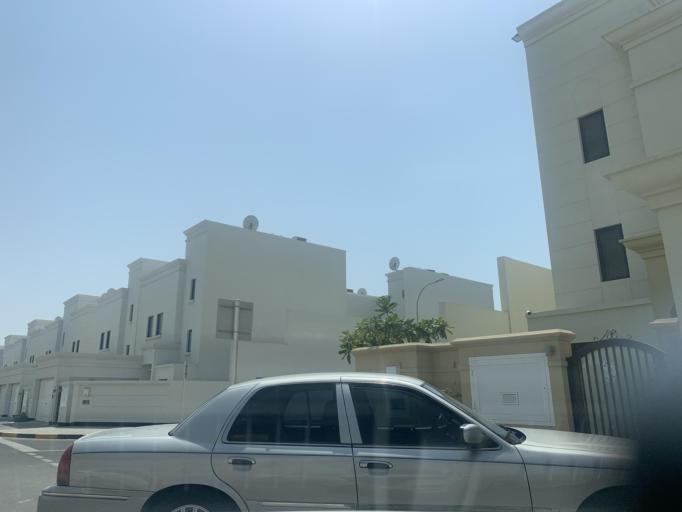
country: BH
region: Muharraq
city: Al Muharraq
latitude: 26.3039
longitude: 50.6285
